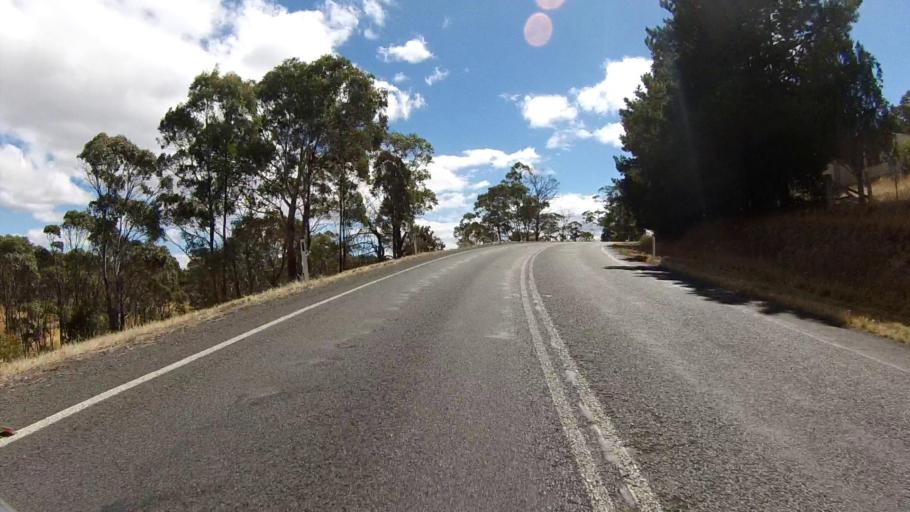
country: AU
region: Tasmania
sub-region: Sorell
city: Sorell
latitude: -42.6222
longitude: 147.6322
